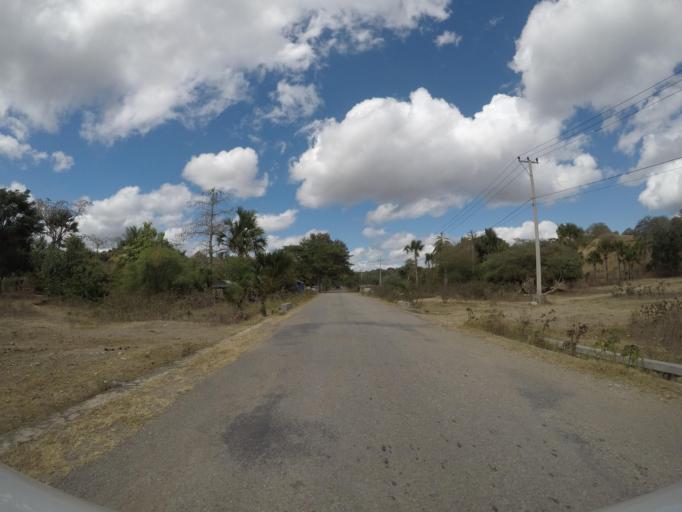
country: TL
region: Lautem
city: Lospalos
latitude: -8.4039
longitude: 126.8302
